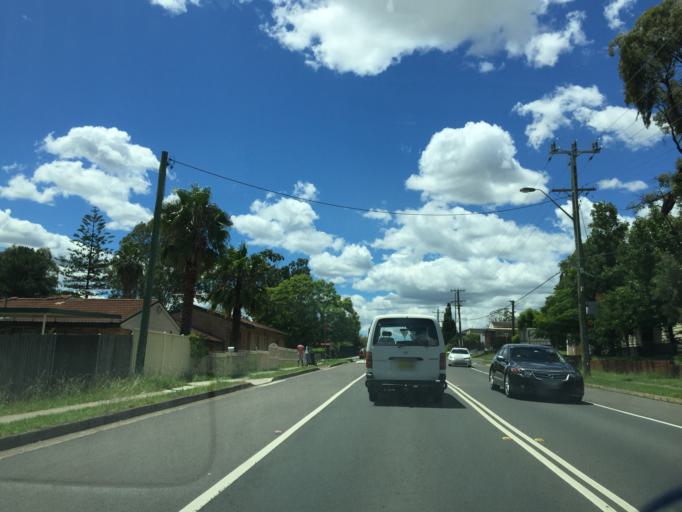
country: AU
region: New South Wales
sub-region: Blacktown
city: Blacktown
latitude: -33.7641
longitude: 150.9160
